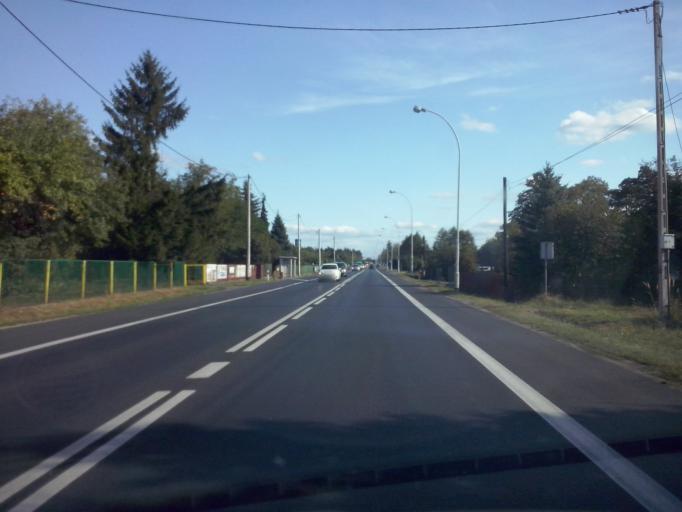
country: PL
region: Subcarpathian Voivodeship
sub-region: Powiat nizanski
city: Nisko
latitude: 50.5370
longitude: 22.1012
